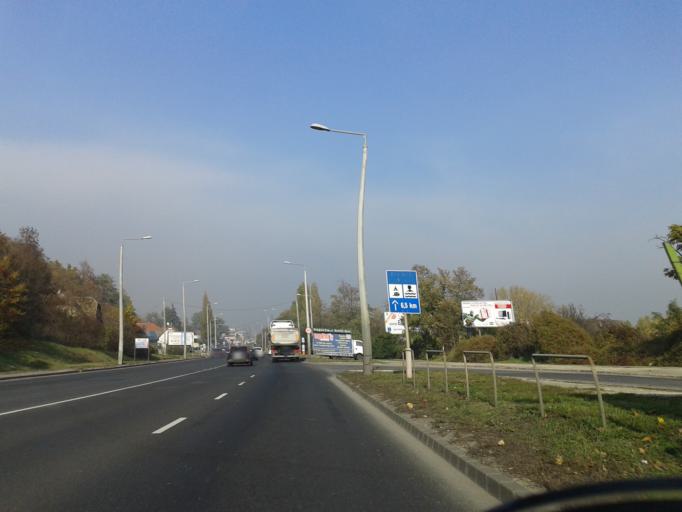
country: HU
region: Budapest
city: Budapest III. keruelet
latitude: 47.5548
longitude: 19.0274
